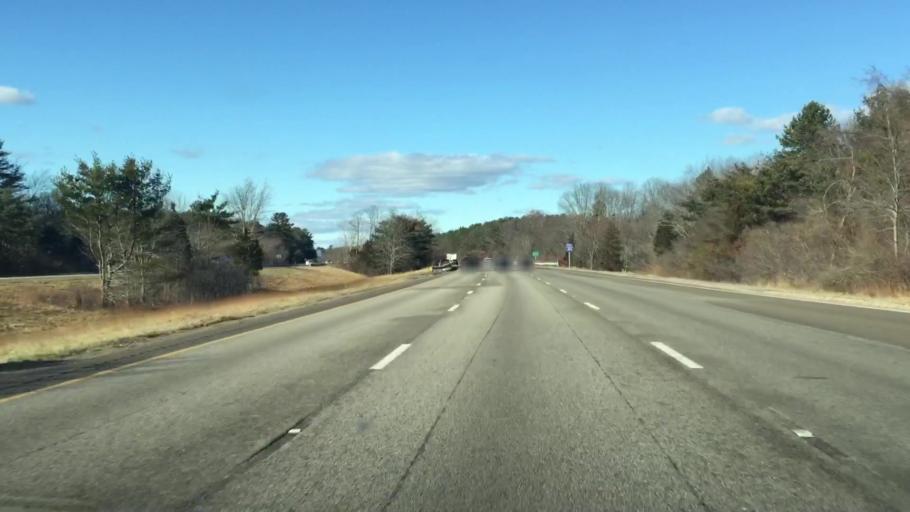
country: US
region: Massachusetts
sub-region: Bristol County
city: Norton Center
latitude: 41.9860
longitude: -71.1633
